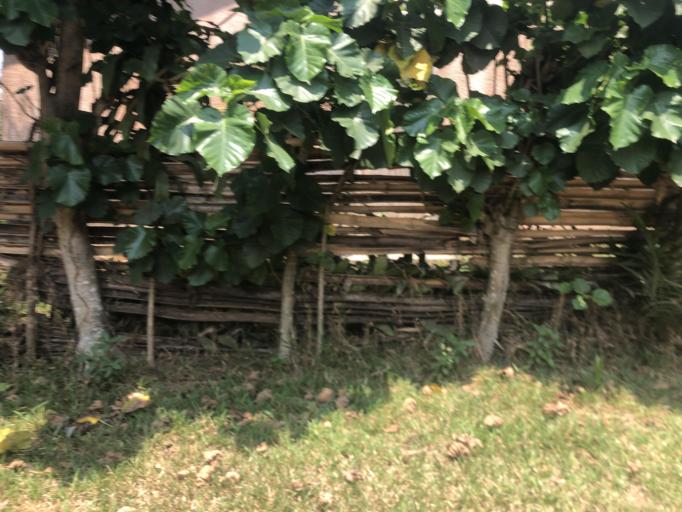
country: CD
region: Bandundu
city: Kikwit
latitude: -5.0699
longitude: 18.8475
